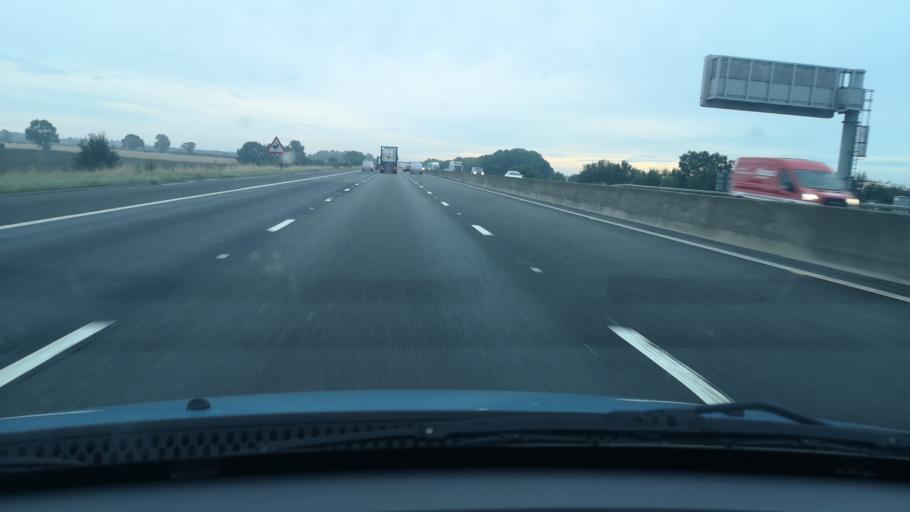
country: GB
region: England
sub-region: East Riding of Yorkshire
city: Rawcliffe
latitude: 53.6592
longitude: -0.9648
